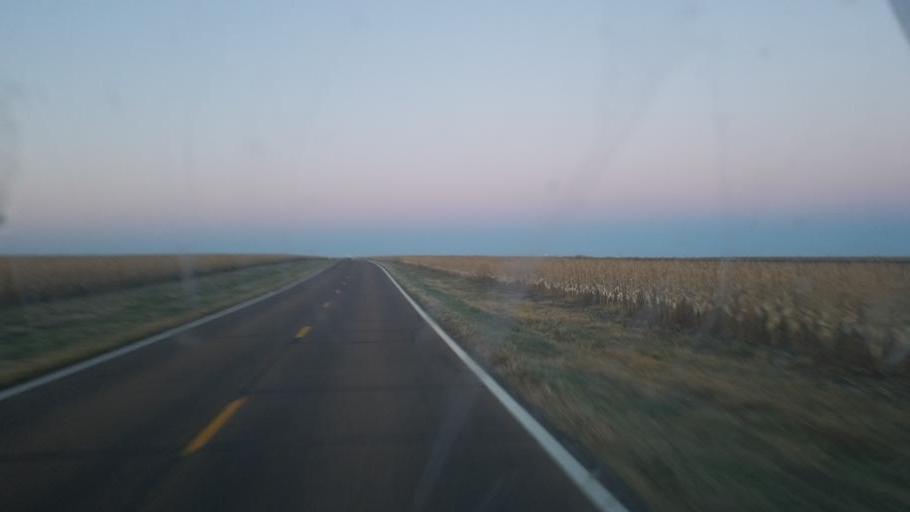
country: US
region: Kansas
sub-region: Wallace County
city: Sharon Springs
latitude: 38.9424
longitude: -101.5116
